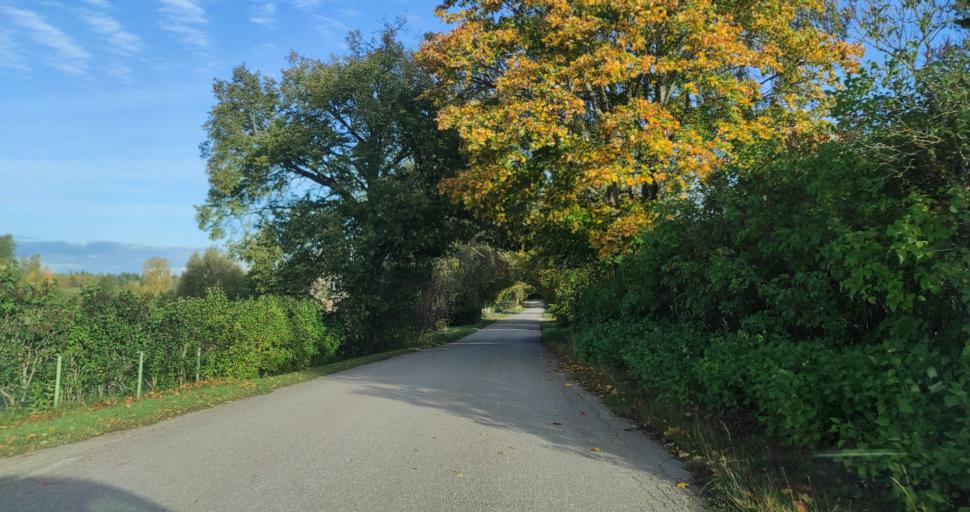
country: LV
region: Skrunda
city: Skrunda
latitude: 56.7429
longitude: 21.8793
